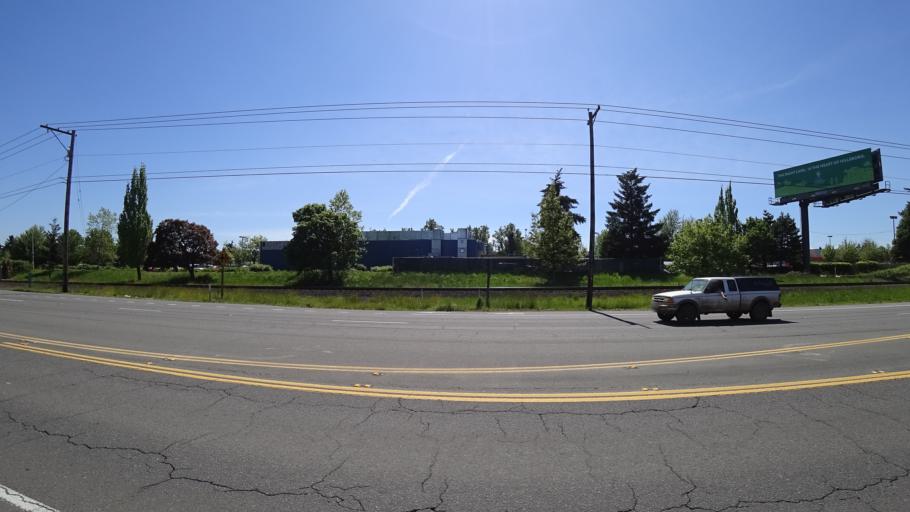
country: US
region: Oregon
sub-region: Washington County
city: Hillsboro
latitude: 45.5049
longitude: -122.9564
